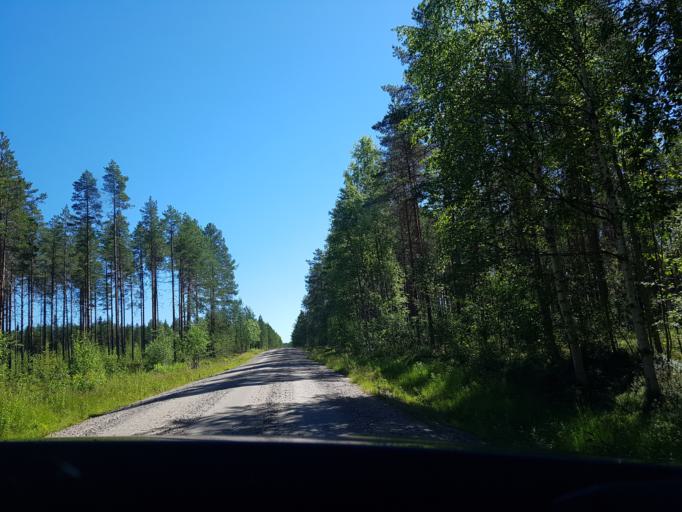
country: FI
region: Kainuu
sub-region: Kehys-Kainuu
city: Kuhmo
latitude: 64.1839
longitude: 29.5835
